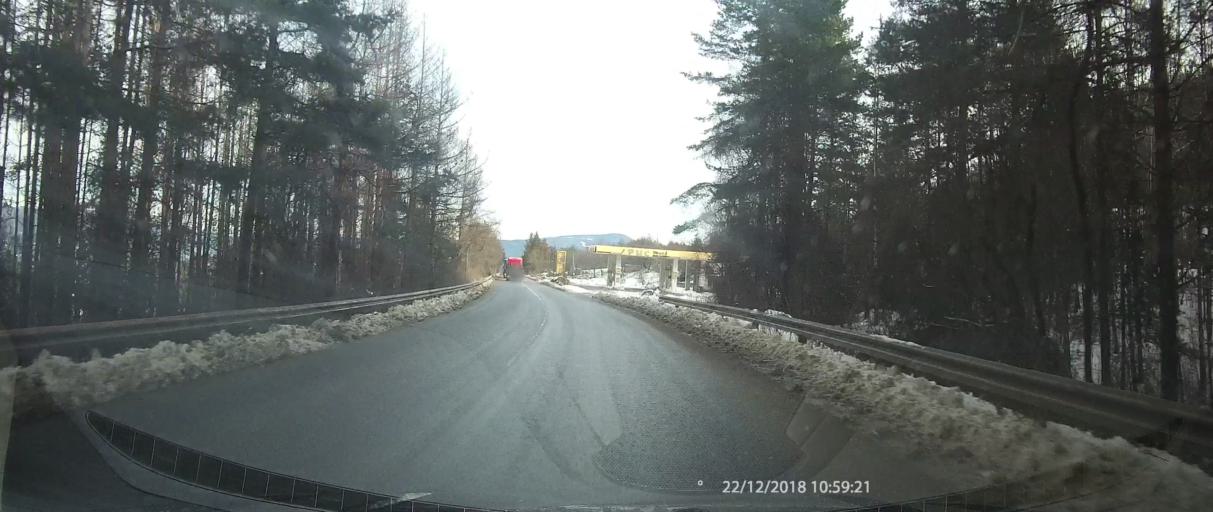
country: MK
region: Kriva Palanka
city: Kriva Palanka
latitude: 42.2240
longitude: 22.4796
